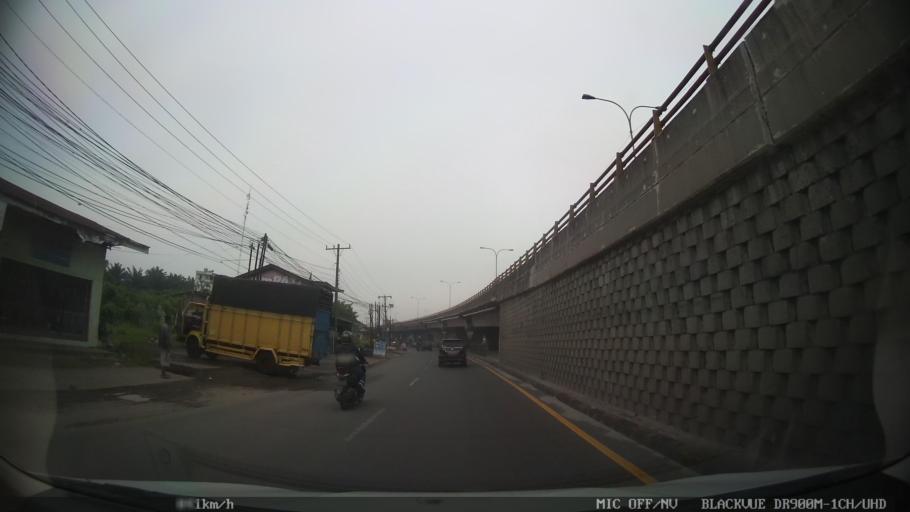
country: ID
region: North Sumatra
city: Deli Tua
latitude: 3.5346
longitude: 98.7222
